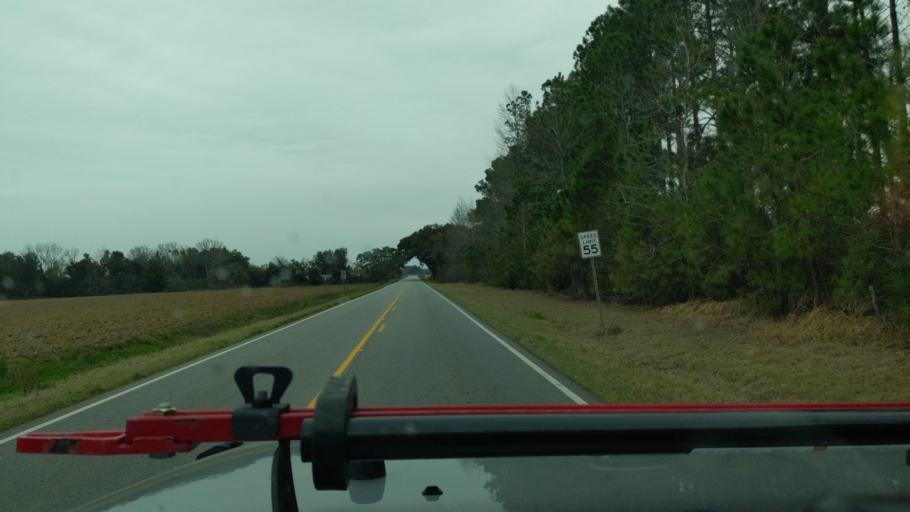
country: US
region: Alabama
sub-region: Baldwin County
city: Foley
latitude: 30.4593
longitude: -87.7423
